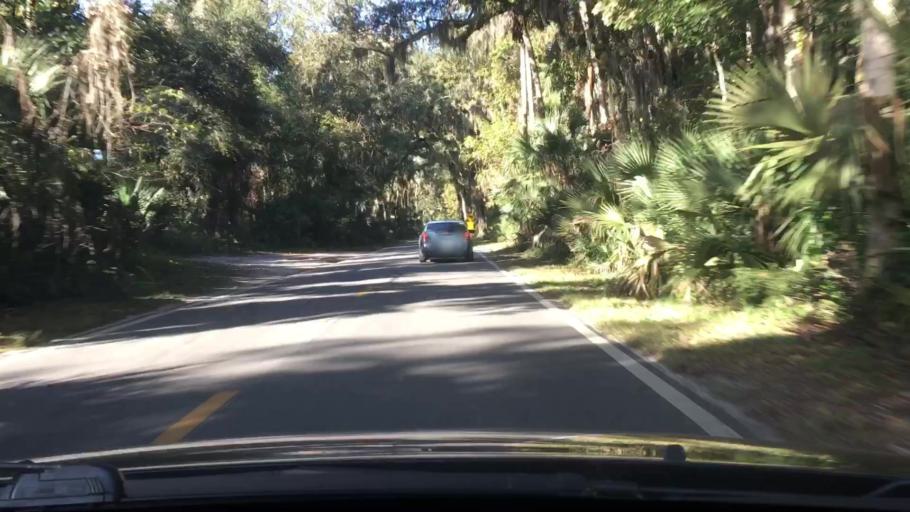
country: US
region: Florida
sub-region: Flagler County
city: Flagler Beach
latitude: 29.4004
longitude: -81.1365
